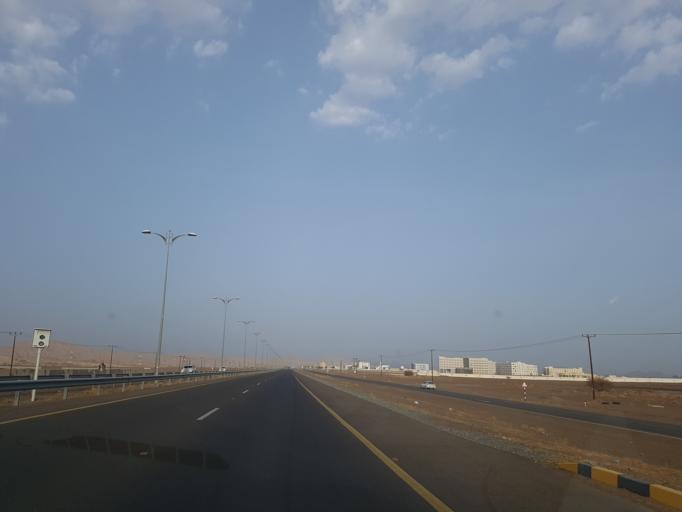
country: OM
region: Al Buraimi
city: Al Buraymi
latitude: 24.2383
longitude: 55.8825
